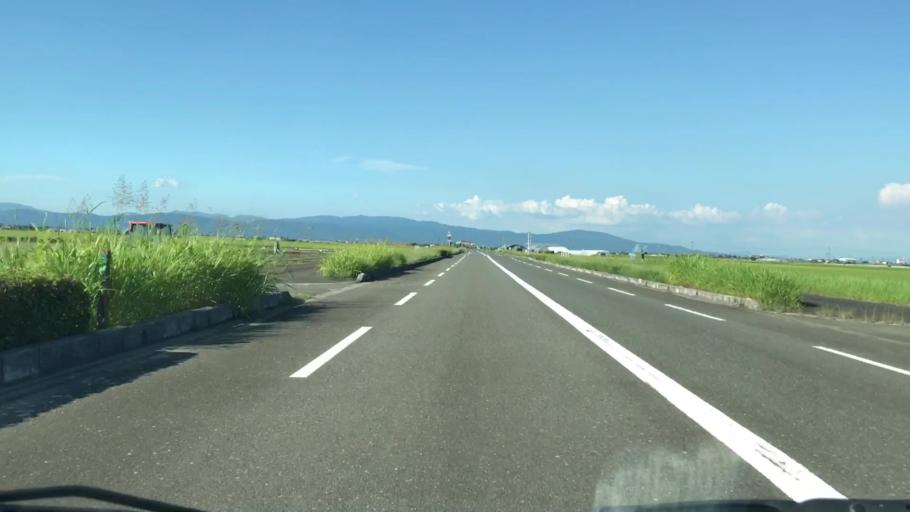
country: JP
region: Saga Prefecture
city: Okawa
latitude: 33.1740
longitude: 130.2961
